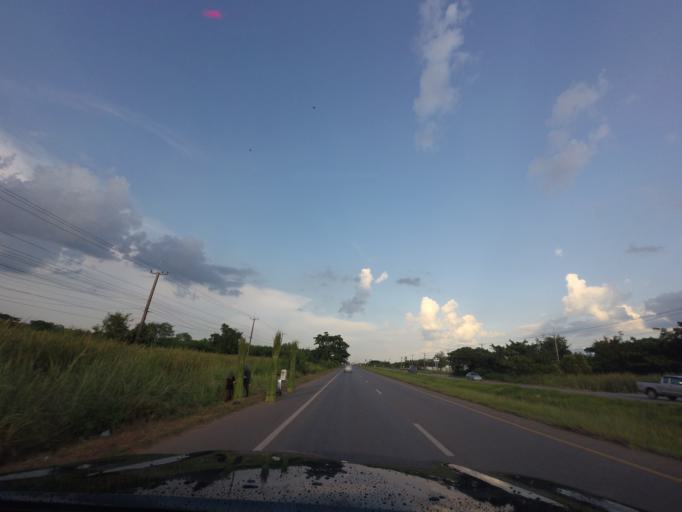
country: TH
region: Khon Kaen
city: Khon Kaen
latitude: 16.3975
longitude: 102.8616
